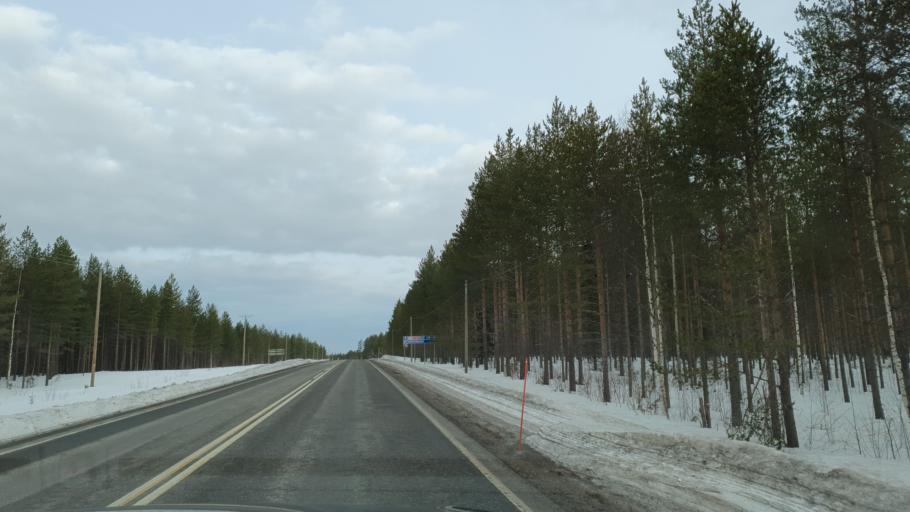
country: FI
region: Kainuu
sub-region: Kajaani
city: Vuokatti
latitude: 64.2127
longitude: 28.1345
